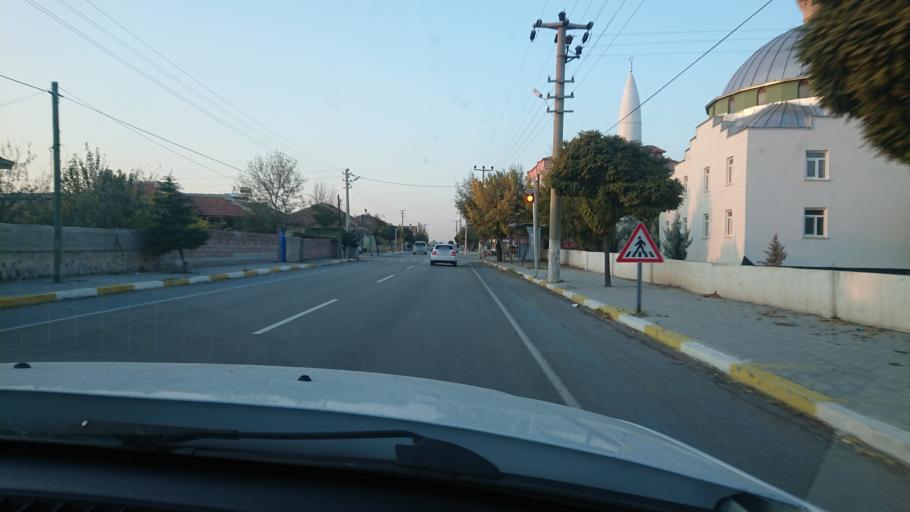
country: TR
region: Aksaray
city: Aksaray
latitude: 38.3071
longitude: 34.0676
